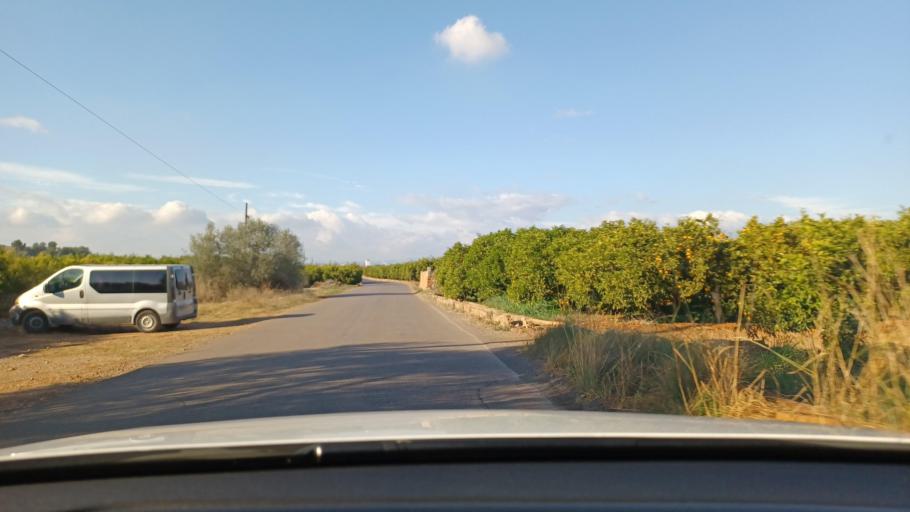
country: ES
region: Valencia
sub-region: Provincia de Castello
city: Betxi
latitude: 39.9403
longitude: -0.2111
